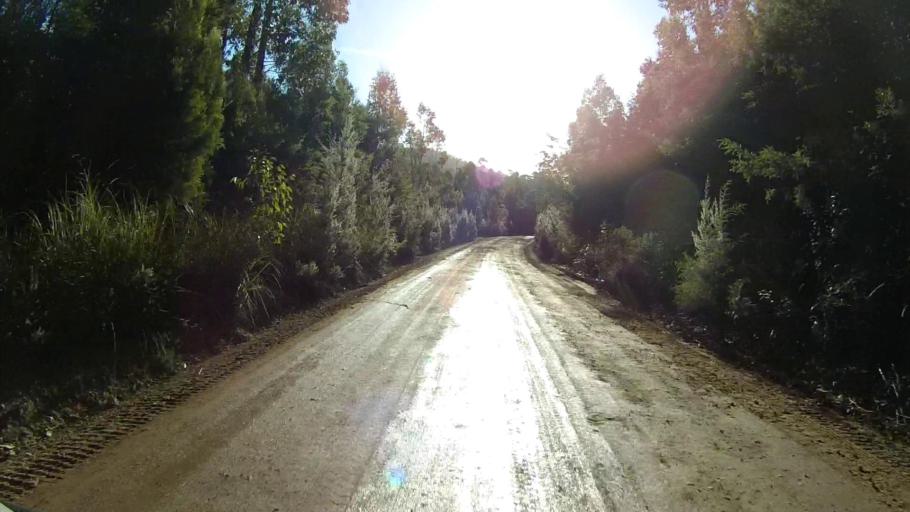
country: AU
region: Tasmania
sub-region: Clarence
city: Sandford
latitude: -43.1366
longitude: 147.9318
